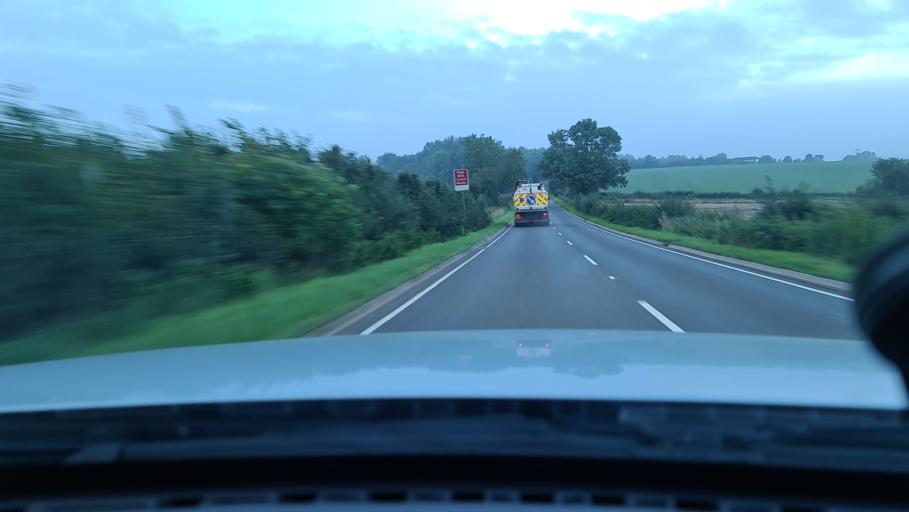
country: GB
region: England
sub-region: Warwickshire
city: Wolston
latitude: 52.3661
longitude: -1.3867
